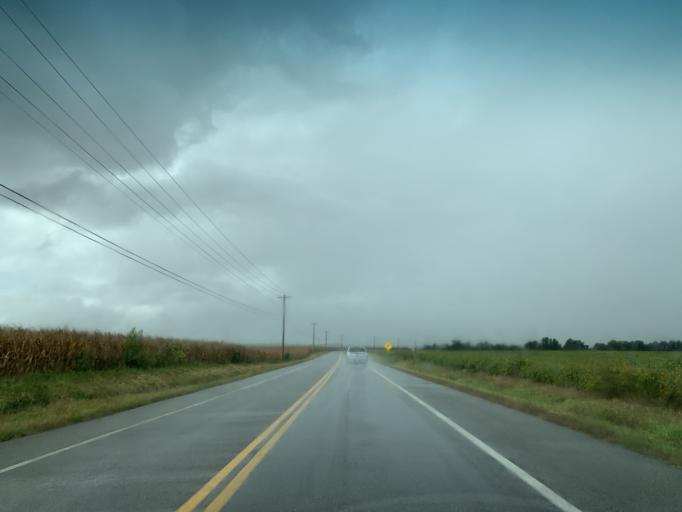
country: US
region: Maryland
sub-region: Queen Anne's County
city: Kingstown
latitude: 39.2031
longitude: -75.8631
